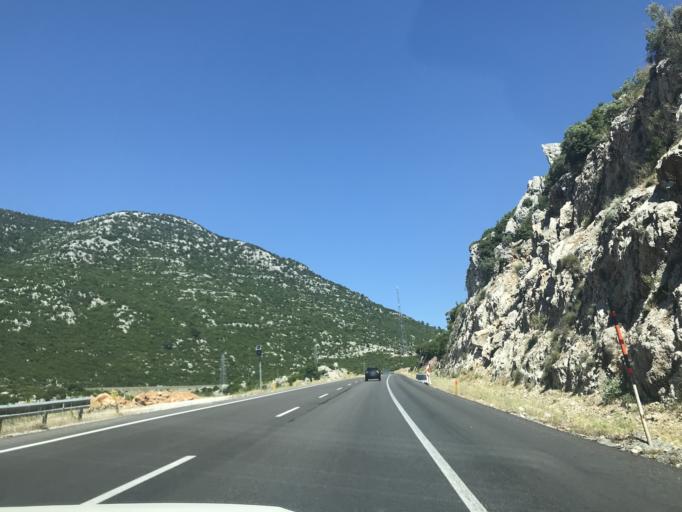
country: TR
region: Antalya
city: Dagbeli
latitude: 37.1634
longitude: 30.5046
